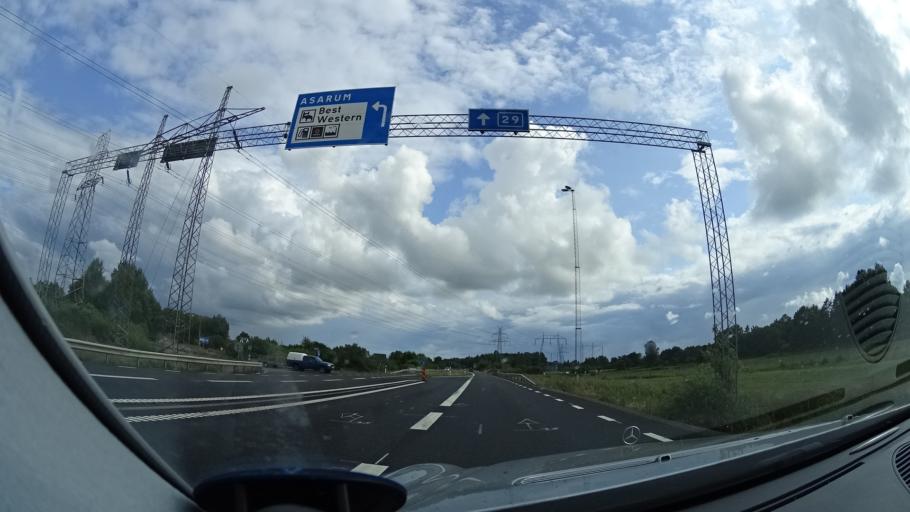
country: SE
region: Blekinge
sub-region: Karlshamns Kommun
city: Karlshamn
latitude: 56.2024
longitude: 14.8113
